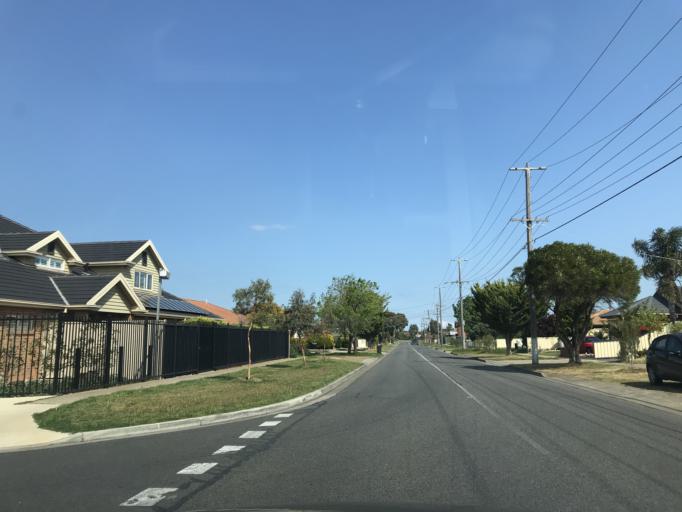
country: AU
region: Victoria
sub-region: Wyndham
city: Hoppers Crossing
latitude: -37.8641
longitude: 144.7104
